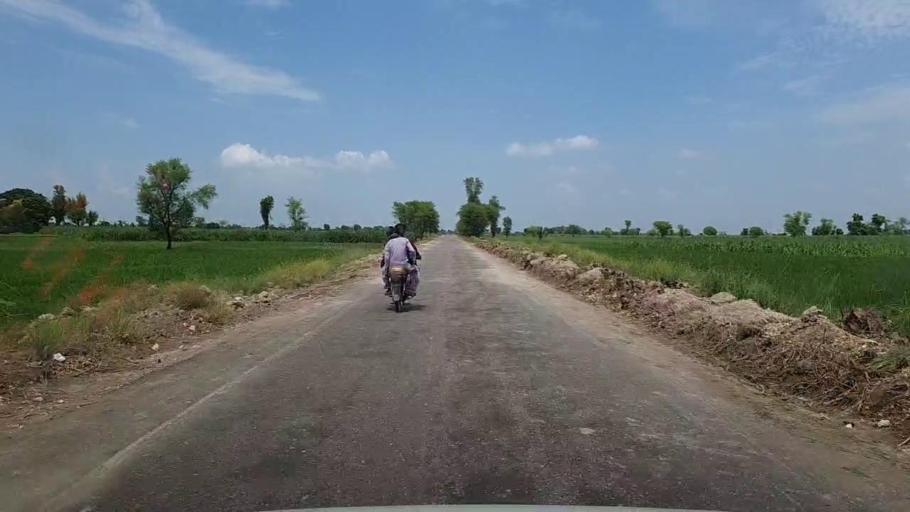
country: PK
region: Sindh
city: Bhiria
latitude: 26.9264
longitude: 68.2100
